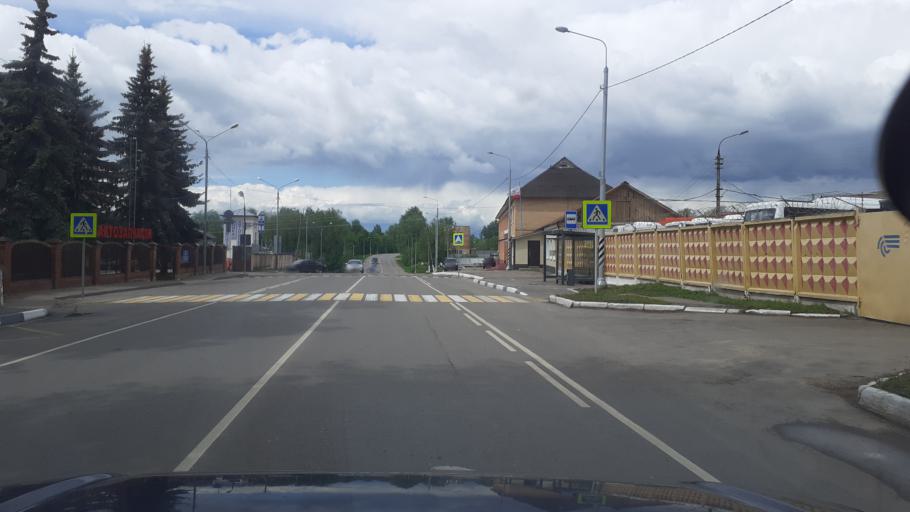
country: RU
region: Moskovskaya
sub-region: Volokolamskiy Rayon
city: Volokolamsk
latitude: 56.0455
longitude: 35.9503
